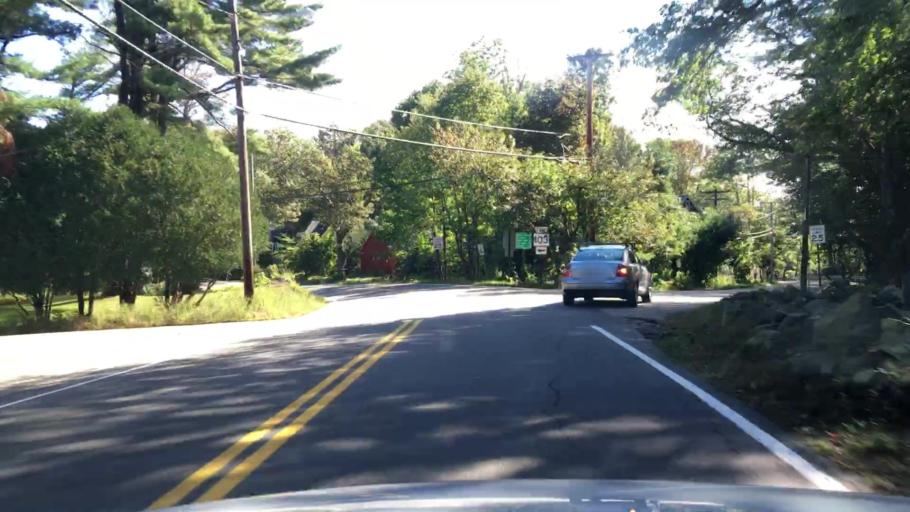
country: US
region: Maine
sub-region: York County
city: Kittery Point
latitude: 43.0852
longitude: -70.6929
